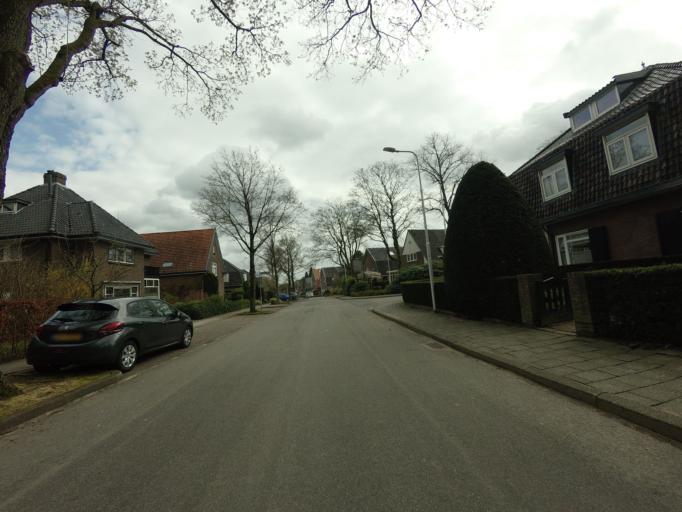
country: NL
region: Gelderland
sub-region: Gemeente Renkum
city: Heelsum
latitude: 51.9817
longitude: 5.7537
